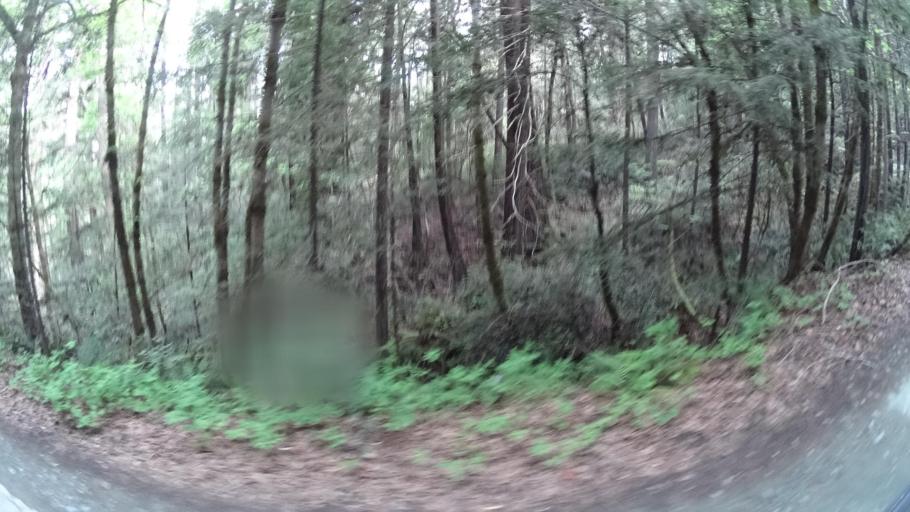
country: US
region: California
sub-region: Humboldt County
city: Redway
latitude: 40.2379
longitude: -123.8142
